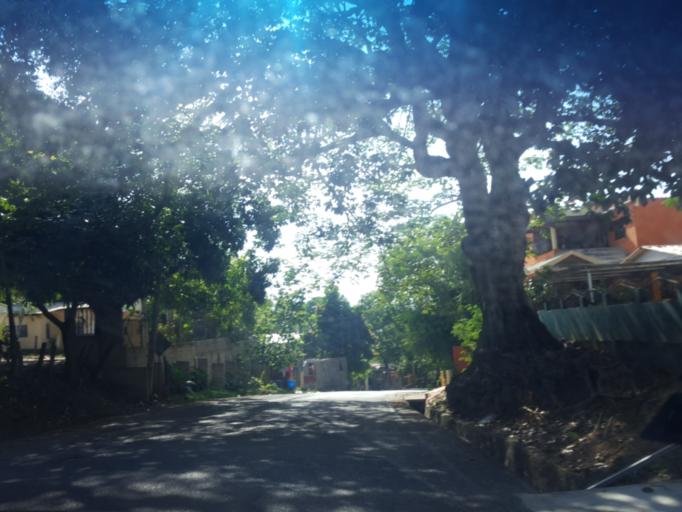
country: DO
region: Santiago
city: Licey al Medio
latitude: 19.3762
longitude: -70.6097
